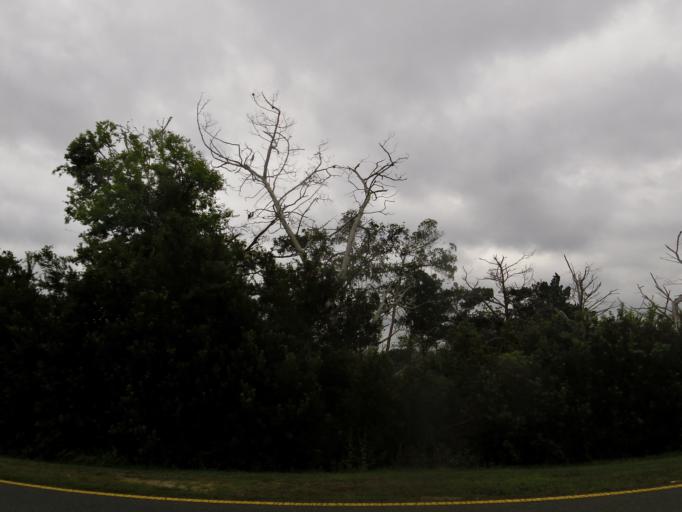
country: US
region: Georgia
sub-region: Glynn County
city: Saint Simon Mills
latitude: 31.1633
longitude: -81.4093
